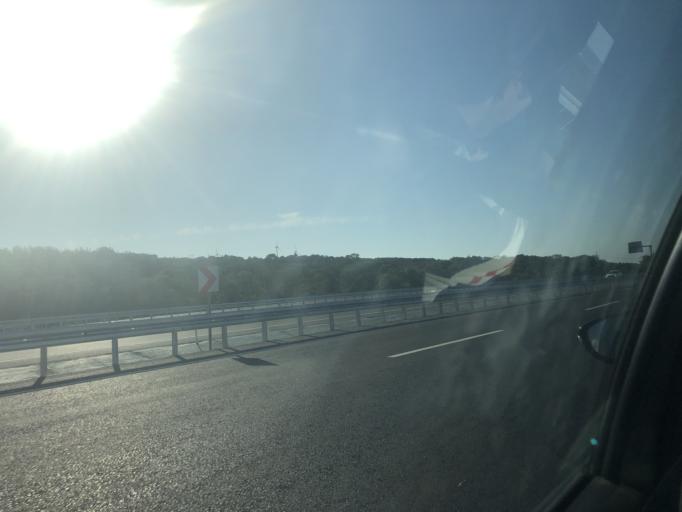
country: TR
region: Istanbul
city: Catalca
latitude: 41.1433
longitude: 28.4769
